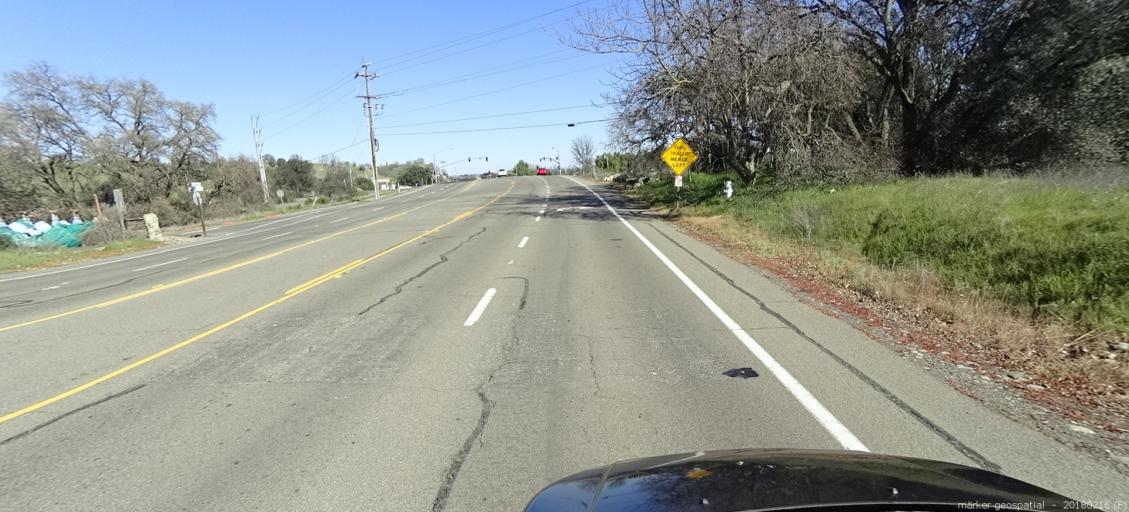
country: US
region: California
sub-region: Sacramento County
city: Gold River
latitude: 38.6322
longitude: -121.2234
